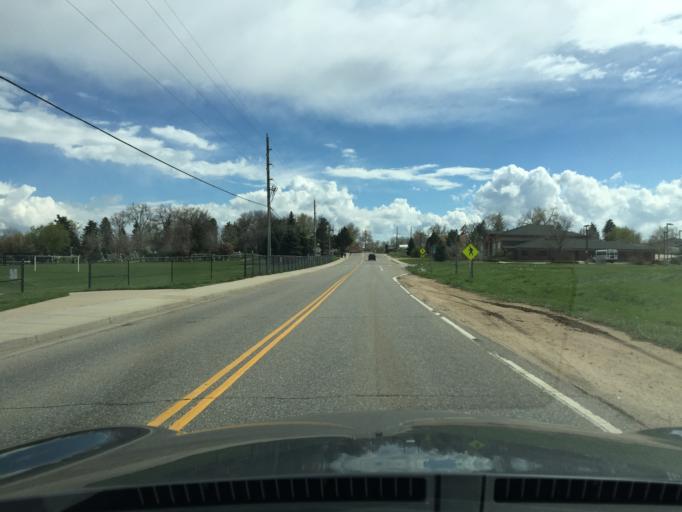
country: US
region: Colorado
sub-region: Boulder County
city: Lafayette
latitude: 40.0031
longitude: -105.0933
